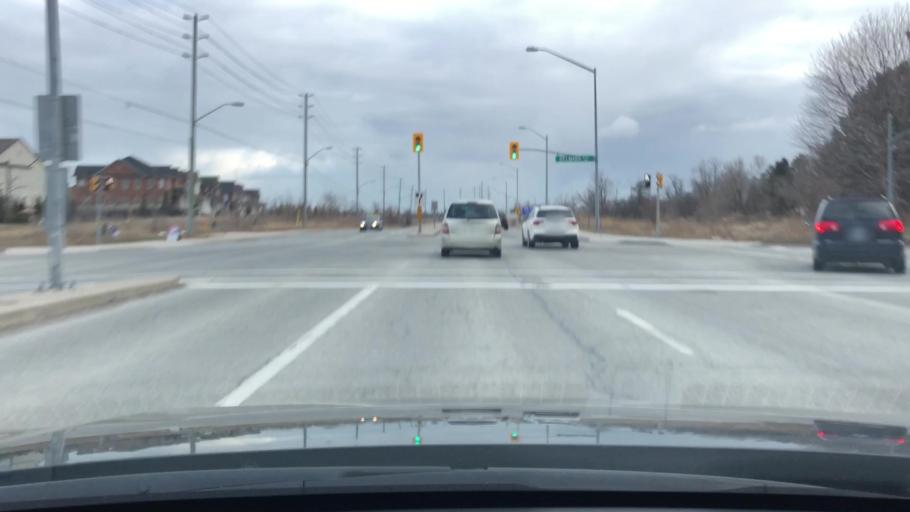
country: CA
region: Ontario
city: Markham
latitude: 43.8759
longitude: -79.2342
